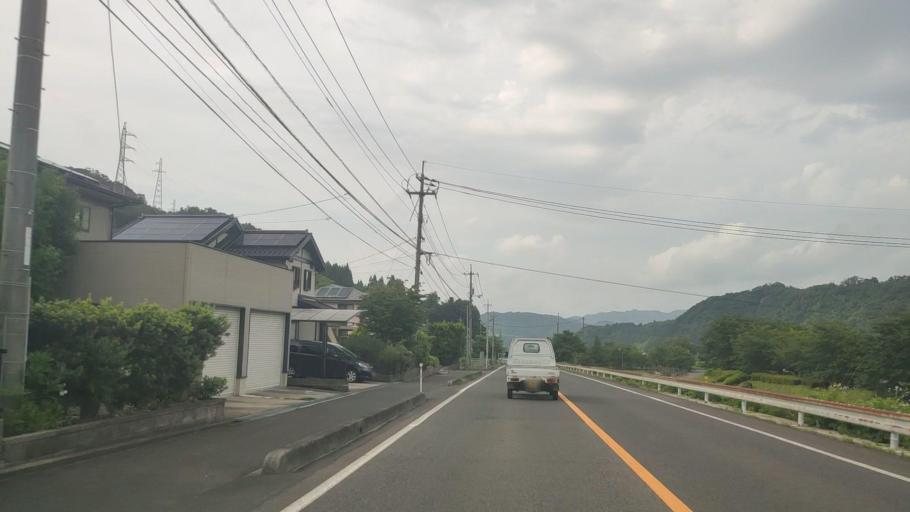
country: JP
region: Tottori
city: Kurayoshi
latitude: 35.3872
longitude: 133.8565
